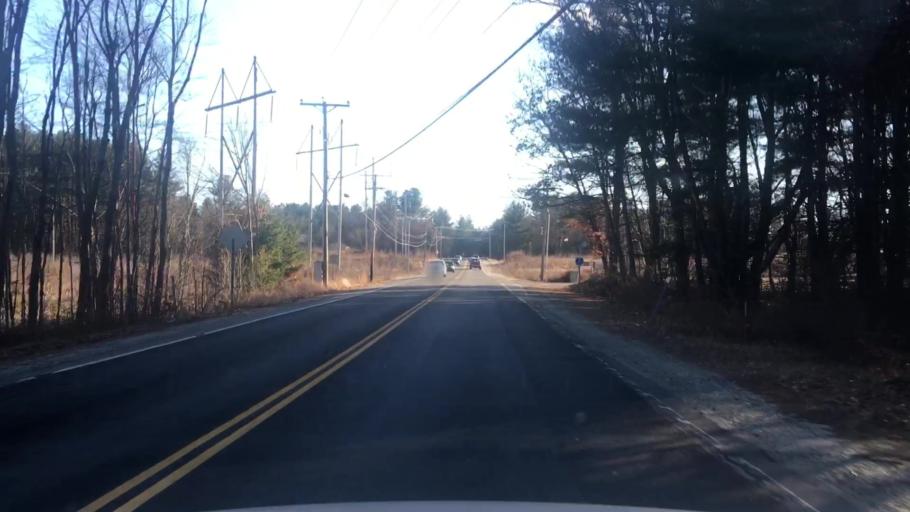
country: US
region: New Hampshire
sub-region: Rockingham County
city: Londonderry
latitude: 42.8822
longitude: -71.3818
